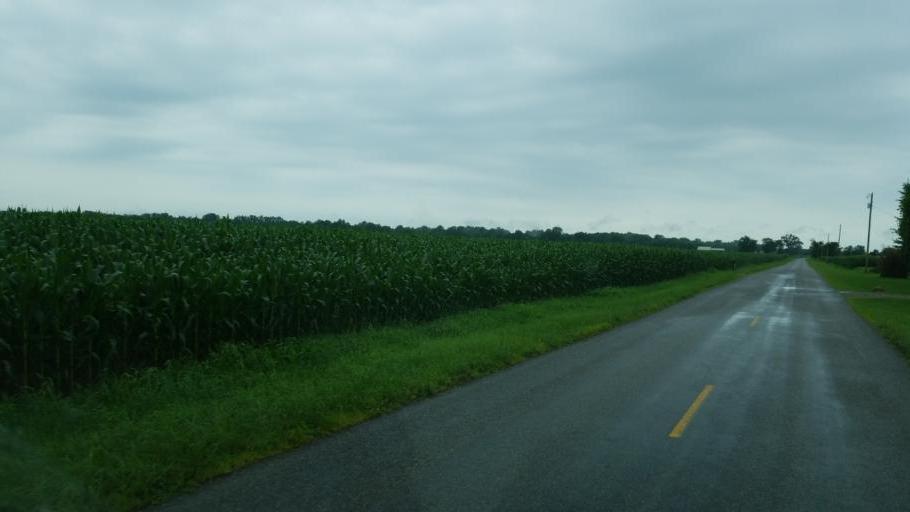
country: US
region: Ohio
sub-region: Union County
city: Richwood
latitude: 40.5117
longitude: -83.4671
